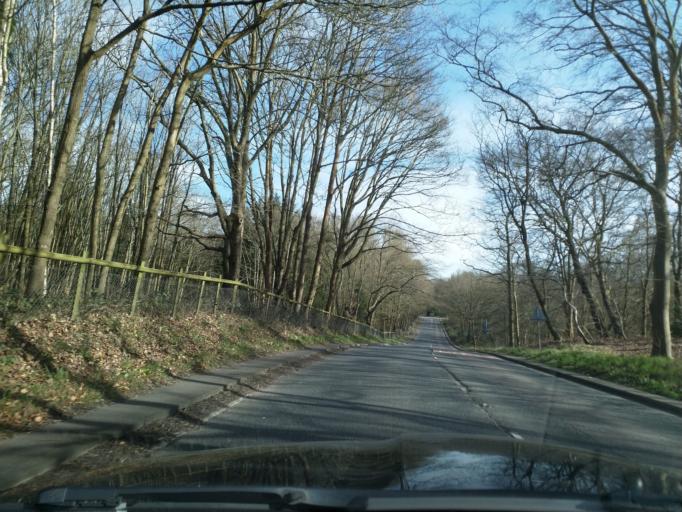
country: GB
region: England
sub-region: Hampshire
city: Aldershot
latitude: 51.2636
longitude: -0.7789
